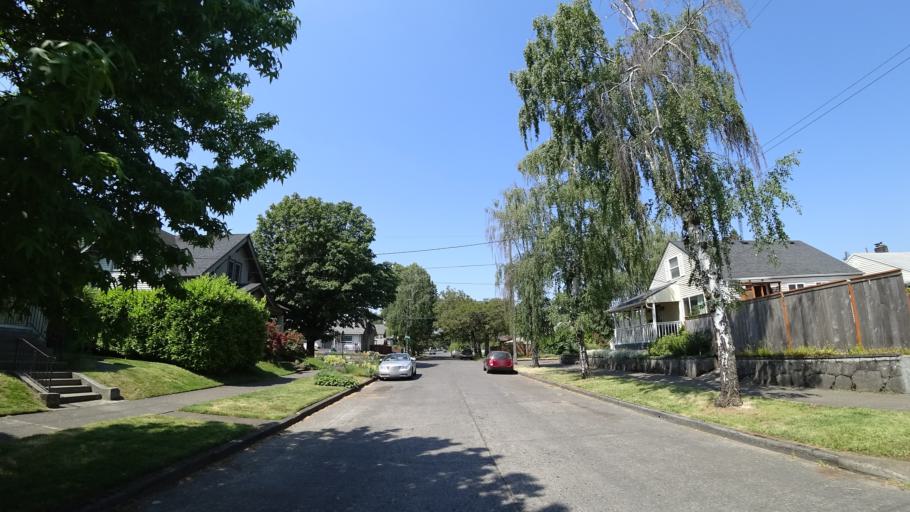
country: US
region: Oregon
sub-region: Multnomah County
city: Portland
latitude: 45.5646
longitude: -122.6518
